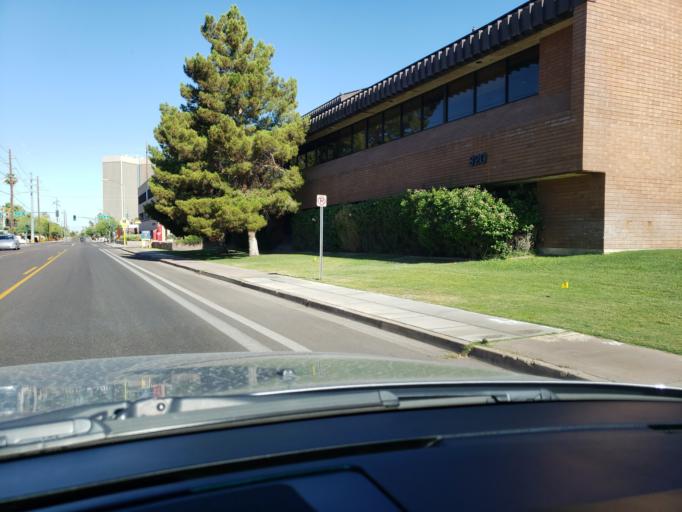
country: US
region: Arizona
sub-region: Maricopa County
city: Phoenix
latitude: 33.4767
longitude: -112.0680
